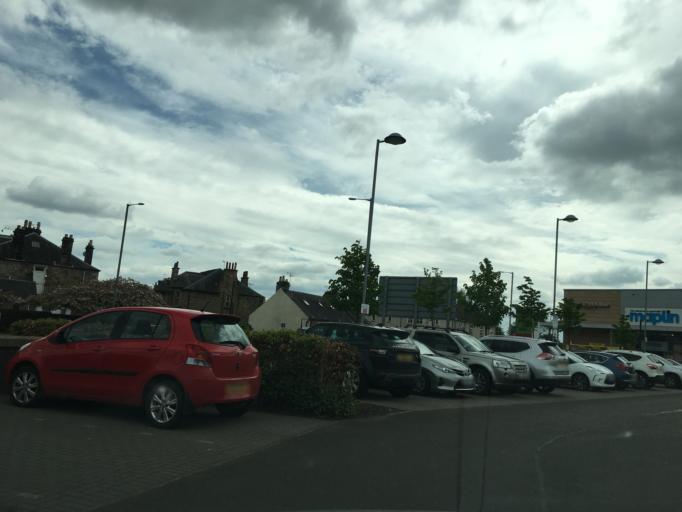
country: GB
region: Scotland
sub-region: Stirling
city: Stirling
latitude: 56.1147
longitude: -3.9330
